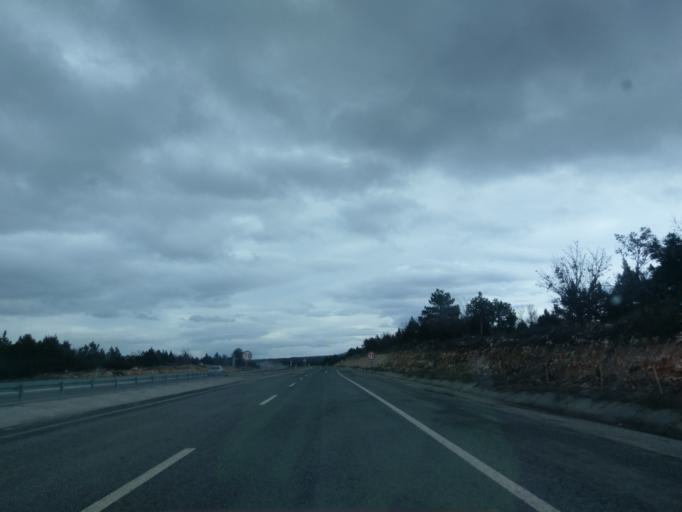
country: TR
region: Kuetahya
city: Cavdarhisar
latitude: 39.2227
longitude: 29.7401
